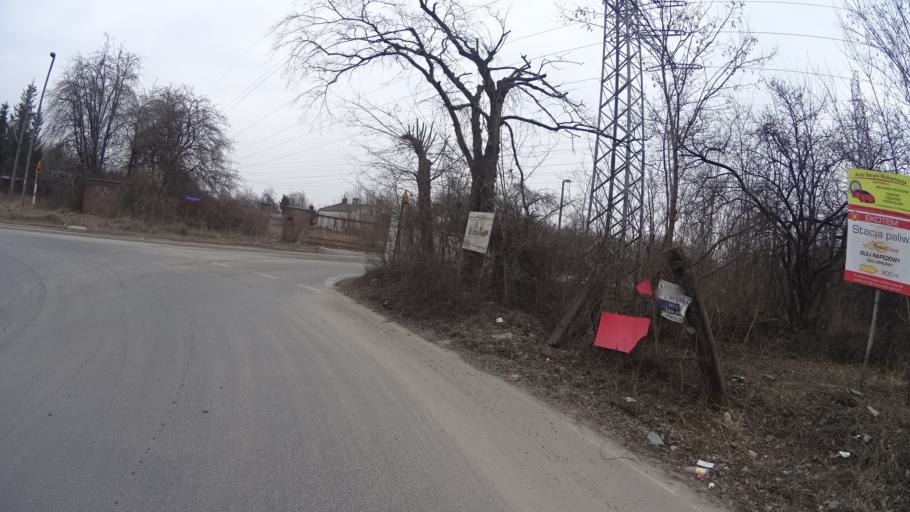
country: PL
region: Masovian Voivodeship
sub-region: Warszawa
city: Ochota
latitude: 52.2192
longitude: 20.9465
